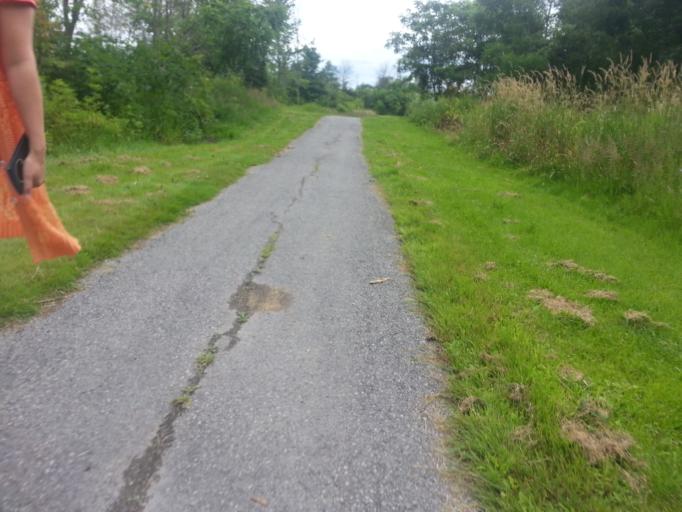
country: CA
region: Ontario
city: Bells Corners
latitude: 45.3343
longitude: -75.9152
